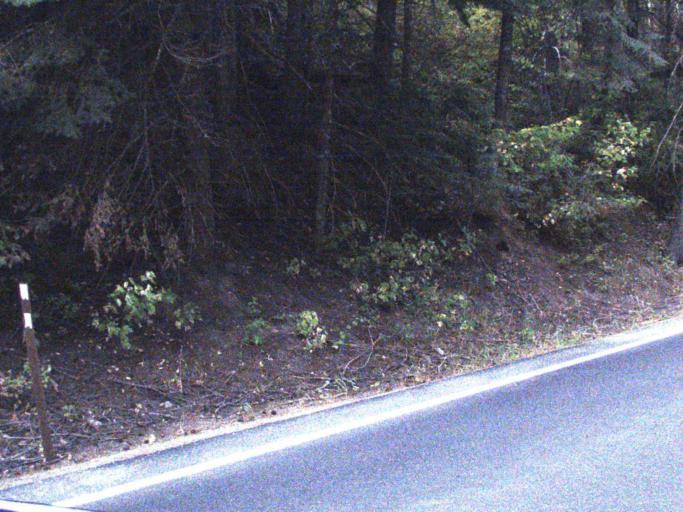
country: US
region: Washington
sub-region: Spokane County
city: Otis Orchards-East Farms
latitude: 47.8653
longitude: -117.1617
